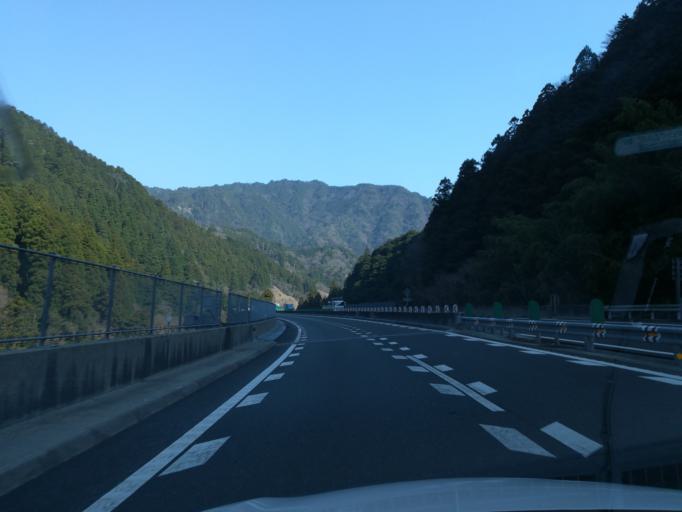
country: JP
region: Ehime
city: Kawanoecho
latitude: 33.9049
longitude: 133.6311
